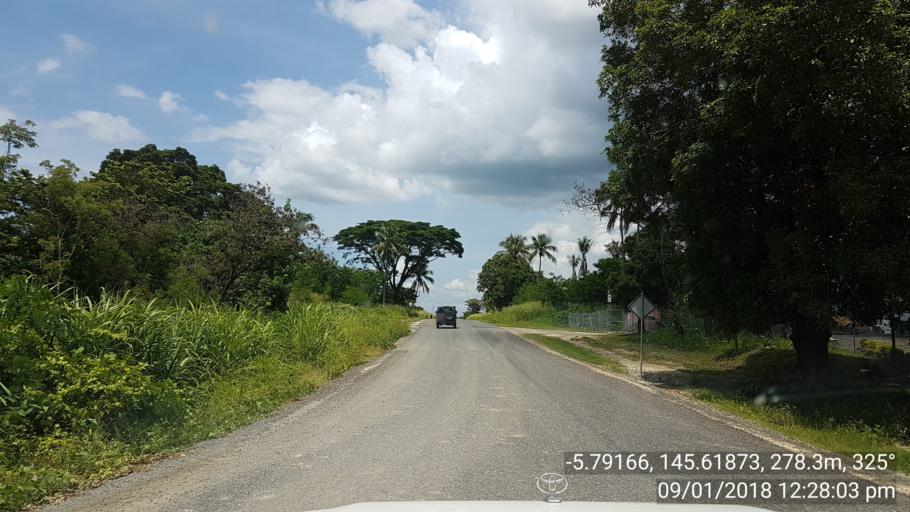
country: PG
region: Eastern Highlands
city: Goroka
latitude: -5.7919
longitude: 145.6186
